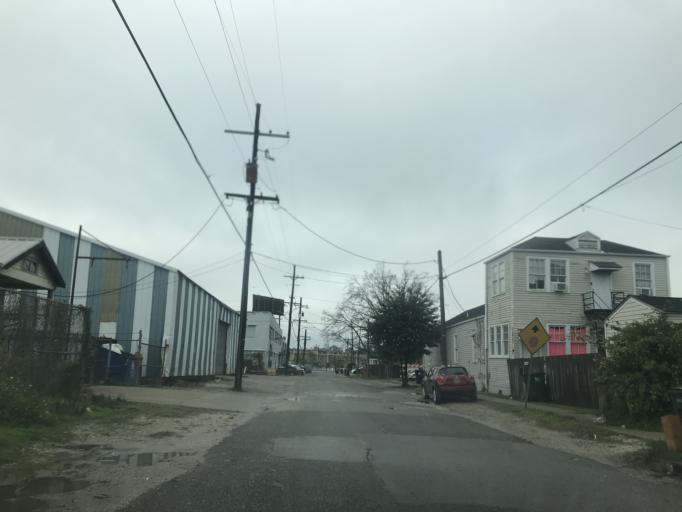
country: US
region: Louisiana
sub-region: Orleans Parish
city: New Orleans
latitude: 29.9735
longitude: -90.1093
